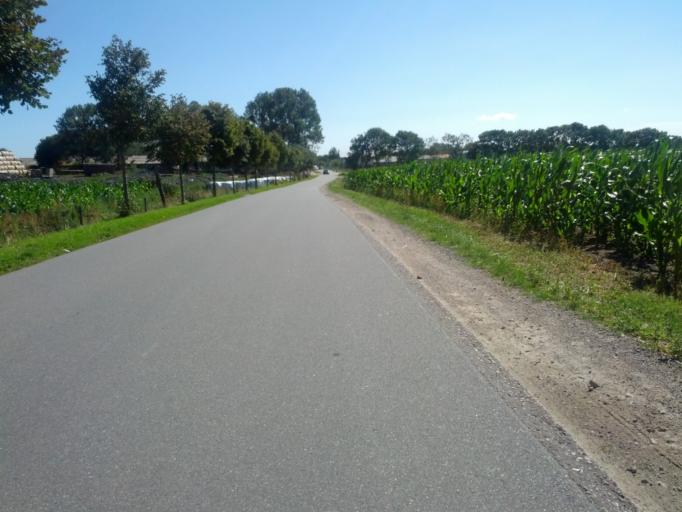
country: DE
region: Mecklenburg-Vorpommern
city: Bastorf
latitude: 54.1277
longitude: 11.6874
